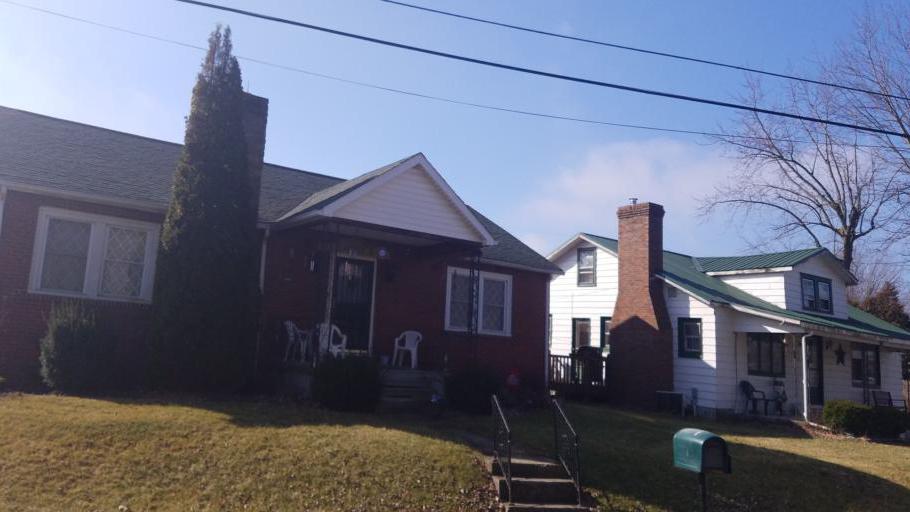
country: US
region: Ohio
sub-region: Crawford County
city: Bucyrus
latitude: 40.7968
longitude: -82.9611
